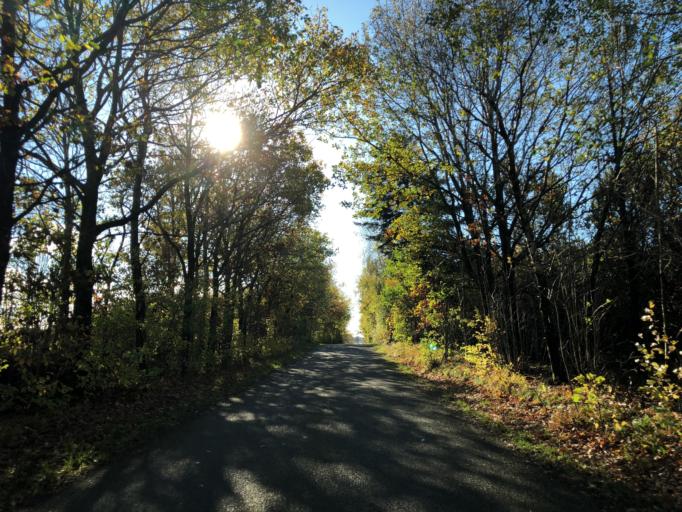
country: DK
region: Central Jutland
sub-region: Herning Kommune
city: Avlum
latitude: 56.2962
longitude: 8.7173
